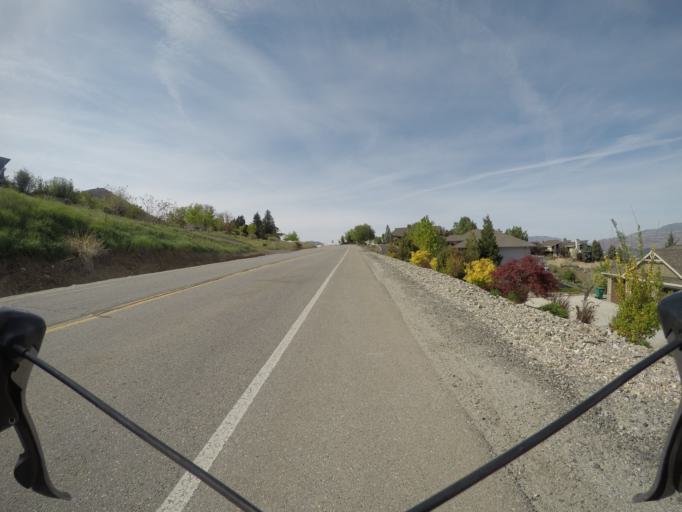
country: US
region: Washington
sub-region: Chelan County
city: Wenatchee
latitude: 47.4107
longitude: -120.3421
